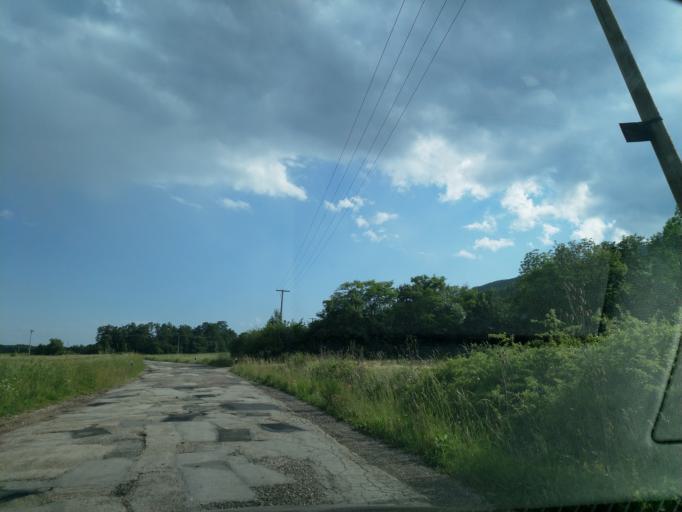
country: RS
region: Central Serbia
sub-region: Borski Okrug
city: Bor
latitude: 43.9880
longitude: 21.9742
